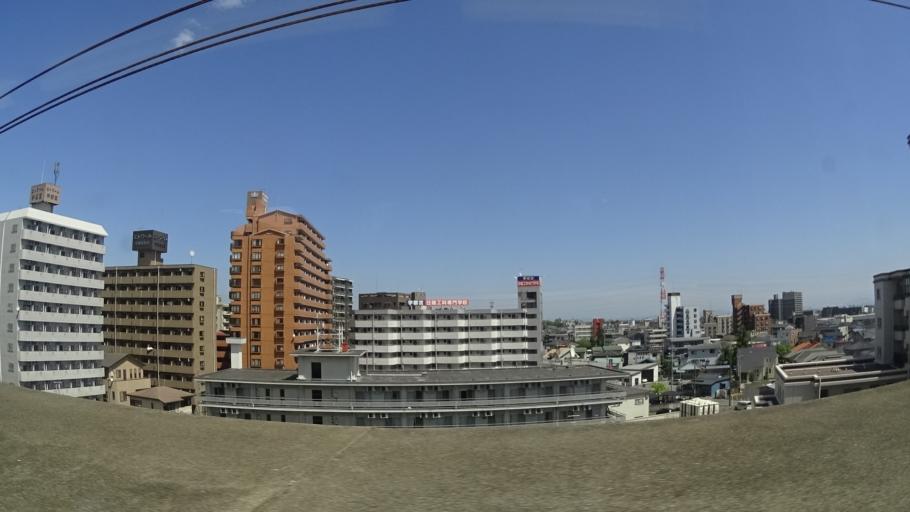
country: JP
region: Tochigi
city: Utsunomiya-shi
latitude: 36.5536
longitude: 139.8969
